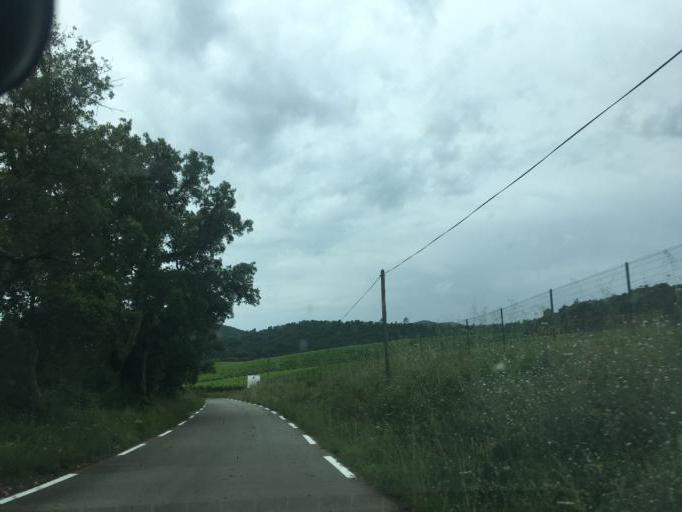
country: FR
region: Provence-Alpes-Cote d'Azur
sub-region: Departement du Var
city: La Londe-les-Maures
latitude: 43.1998
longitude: 6.2125
